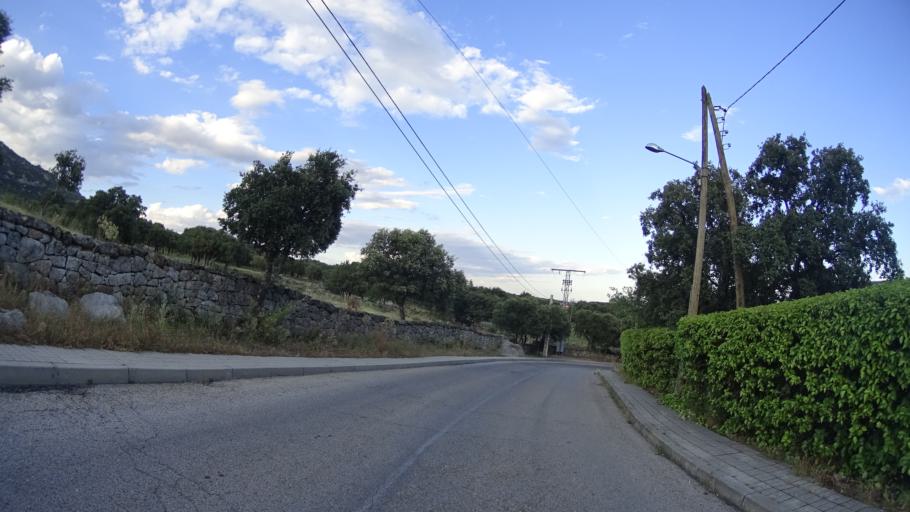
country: ES
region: Madrid
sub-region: Provincia de Madrid
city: Hoyo de Manzanares
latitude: 40.6275
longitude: -3.9079
